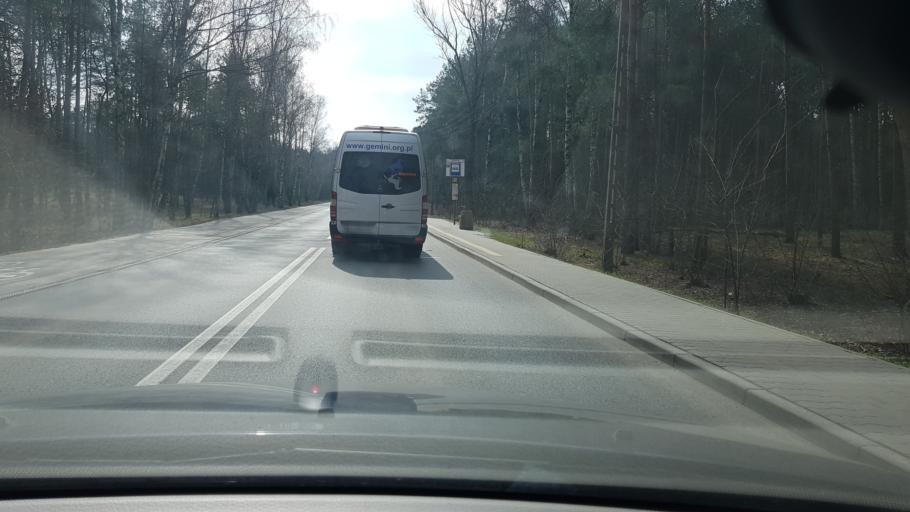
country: PL
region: Masovian Voivodeship
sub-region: Warszawa
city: Wesola
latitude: 52.2322
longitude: 21.2244
